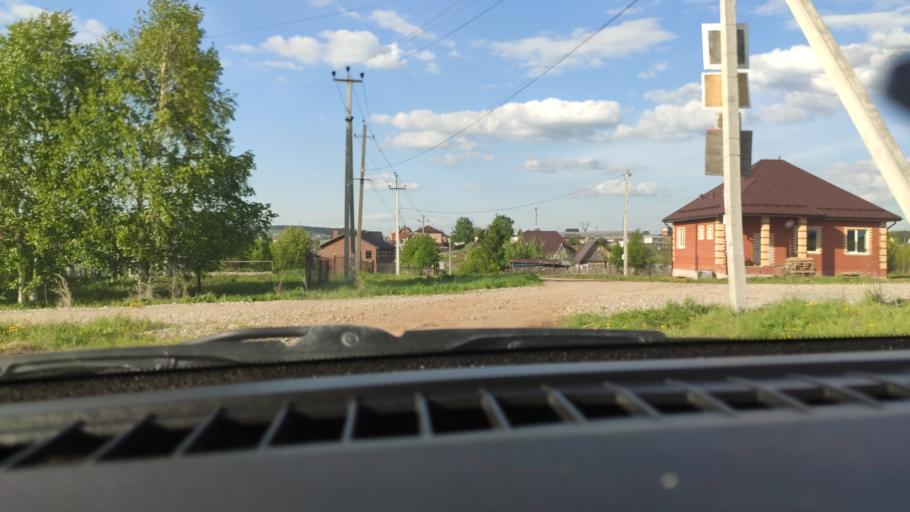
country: RU
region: Perm
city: Ferma
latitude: 57.9393
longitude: 56.3563
